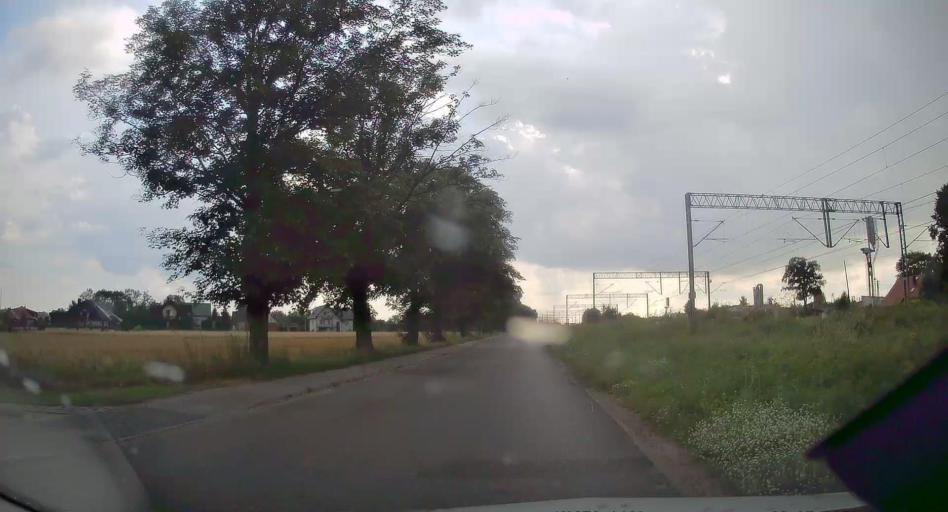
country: PL
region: Lodz Voivodeship
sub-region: Powiat brzezinski
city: Rogow
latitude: 51.8208
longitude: 19.8903
